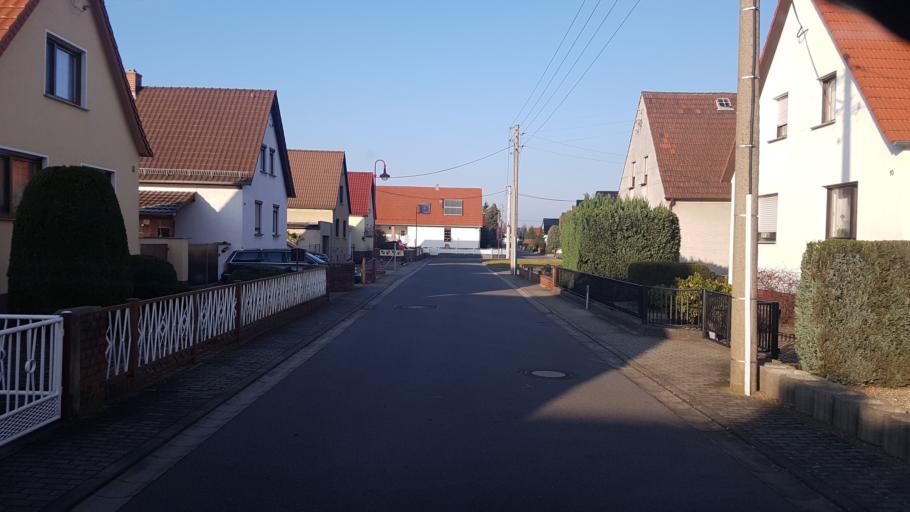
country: DE
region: Brandenburg
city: Lauchhammer
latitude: 51.4704
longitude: 13.7633
